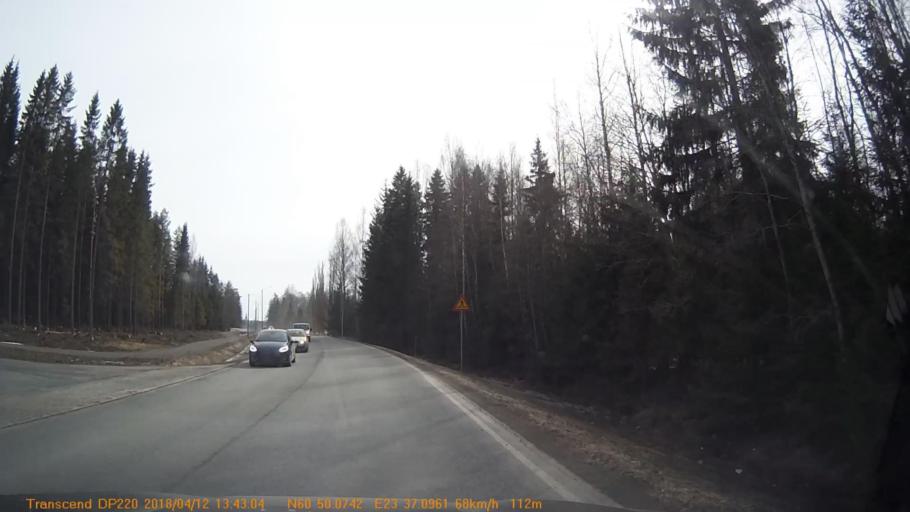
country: FI
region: Haeme
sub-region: Forssa
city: Forssa
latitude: 60.8340
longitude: 23.6184
